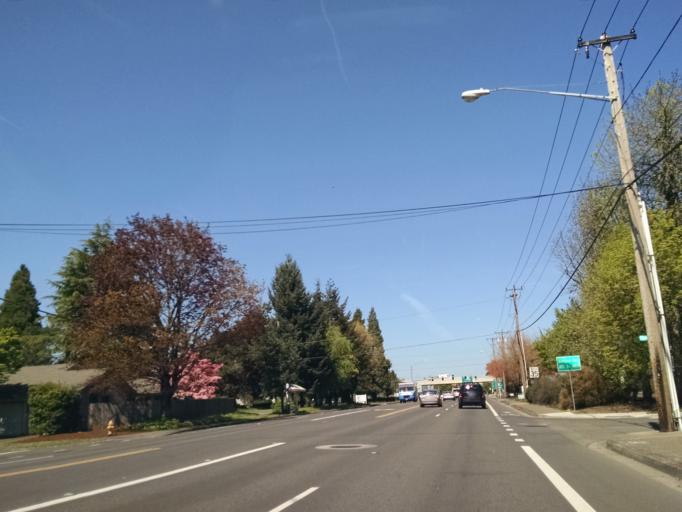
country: US
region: Oregon
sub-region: Lane County
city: Eugene
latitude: 44.0848
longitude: -123.0675
